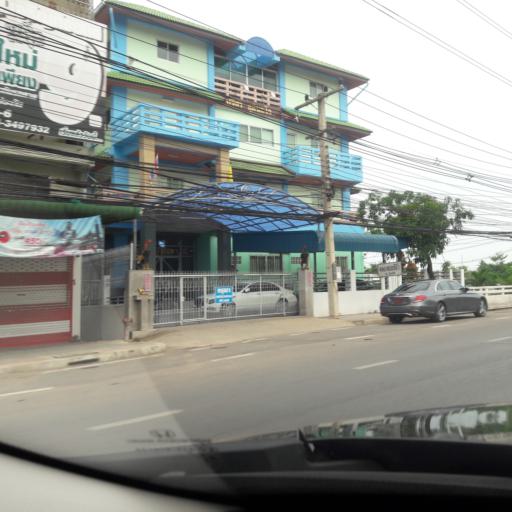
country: TH
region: Ratchaburi
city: Damnoen Saduak
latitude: 13.5334
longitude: 99.9662
